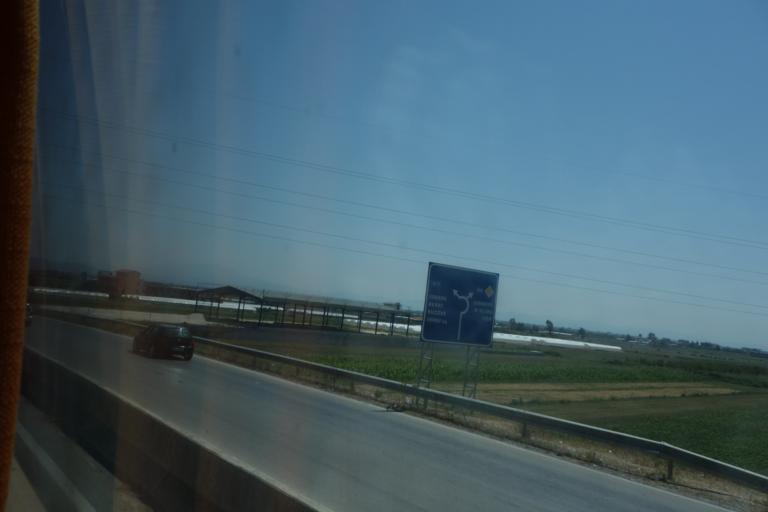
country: AL
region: Fier
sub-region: Rrethi i Lushnjes
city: Karbunara e Vogel
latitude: 40.9230
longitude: 19.6987
